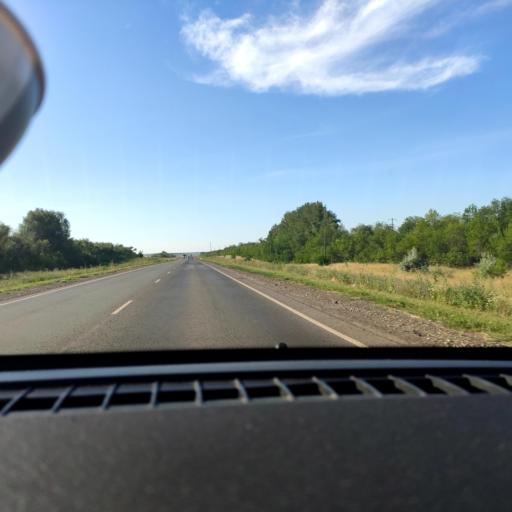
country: RU
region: Samara
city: Krasnoarmeyskoye
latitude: 52.8704
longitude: 49.9855
